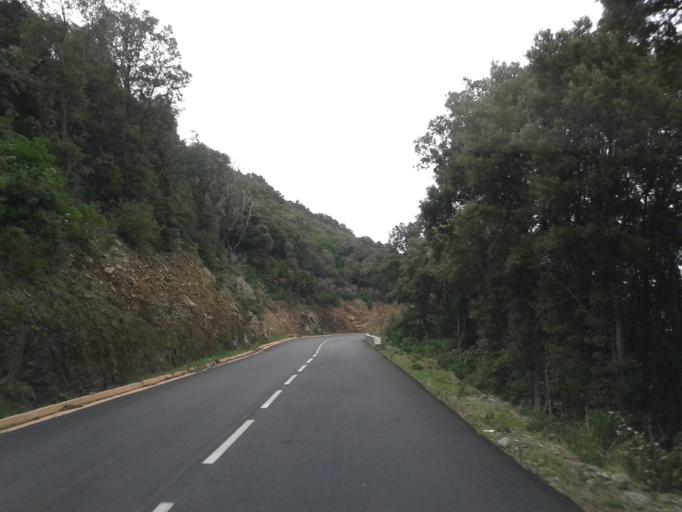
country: FR
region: Corsica
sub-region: Departement de la Haute-Corse
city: Brando
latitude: 42.9743
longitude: 9.3855
